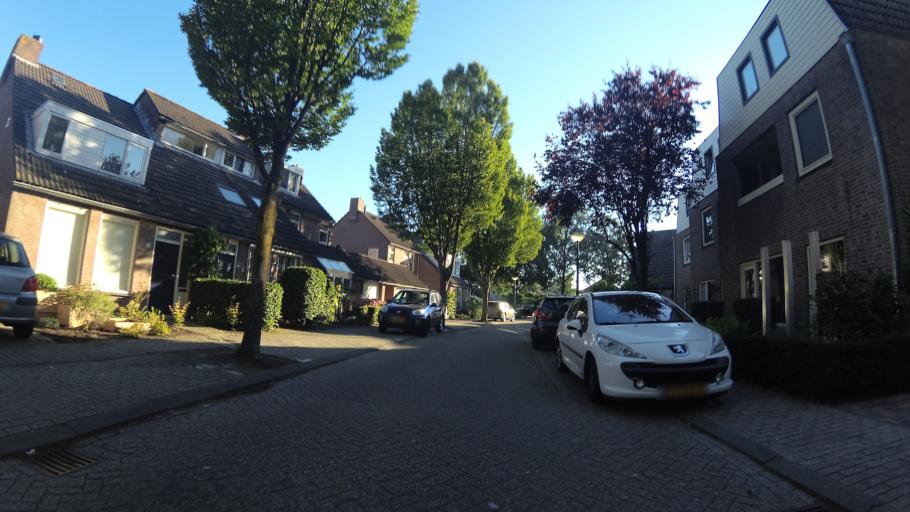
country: NL
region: North Brabant
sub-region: Gemeente Waalwijk
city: Waalwijk
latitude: 51.6546
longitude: 5.0369
